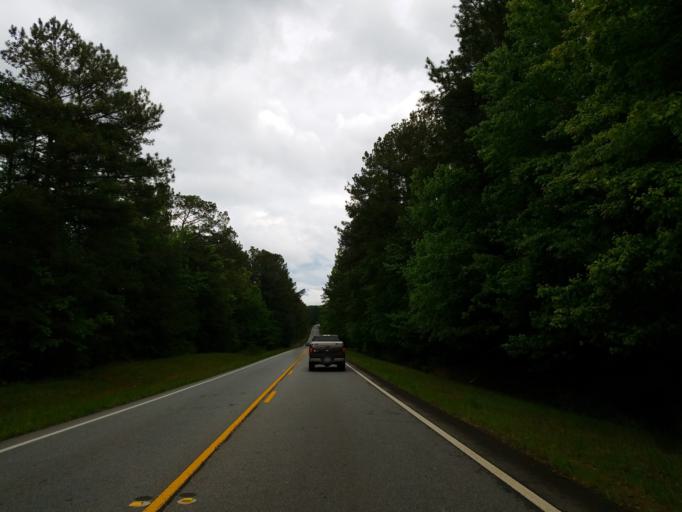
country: US
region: Georgia
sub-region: Crawford County
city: Roberta
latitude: 32.8444
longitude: -84.0701
